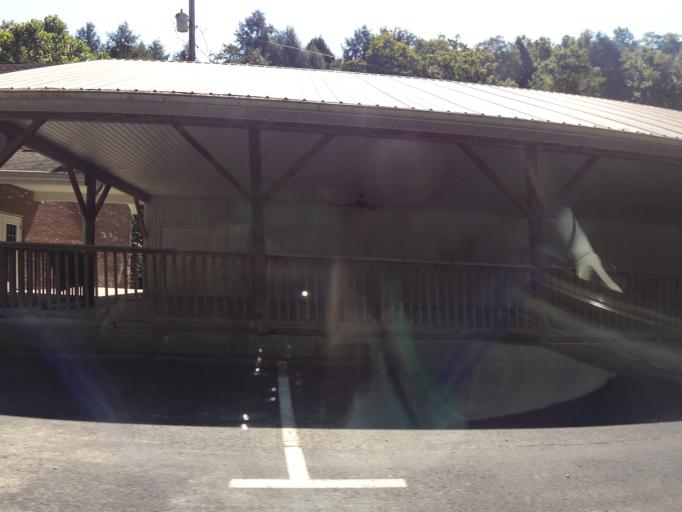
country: US
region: Kentucky
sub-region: Leslie County
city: Hyden
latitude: 37.1393
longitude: -83.4385
